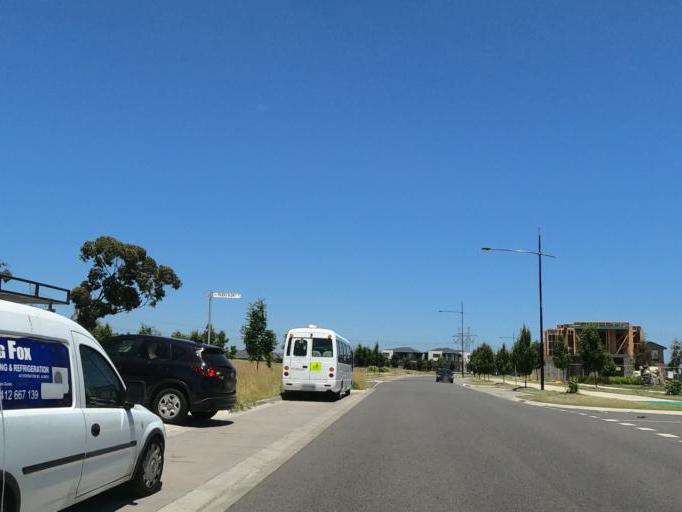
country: AU
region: Victoria
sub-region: Hume
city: Roxburgh Park
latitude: -37.6239
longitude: 144.9169
